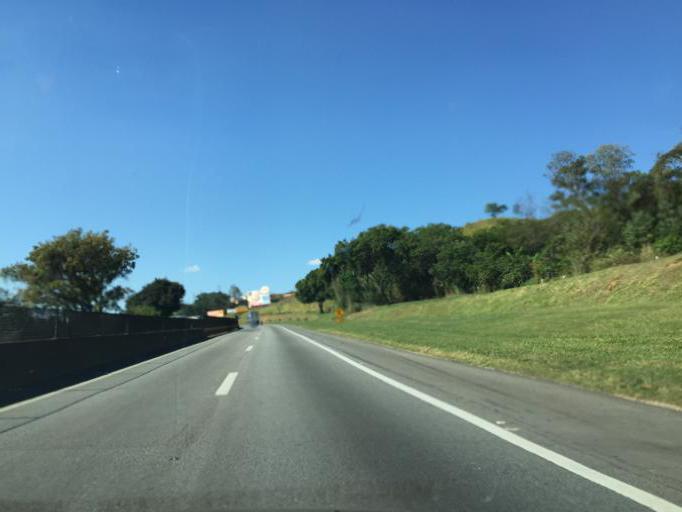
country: BR
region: Sao Paulo
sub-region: Guaratingueta
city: Guaratingueta
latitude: -22.8198
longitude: -45.1854
